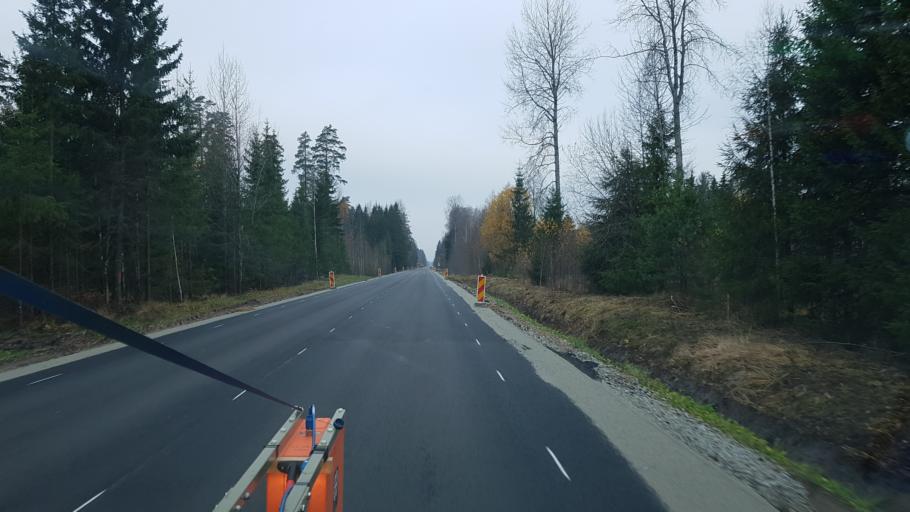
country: EE
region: Paernumaa
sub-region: Vaendra vald (alev)
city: Vandra
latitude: 58.8283
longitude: 25.1125
